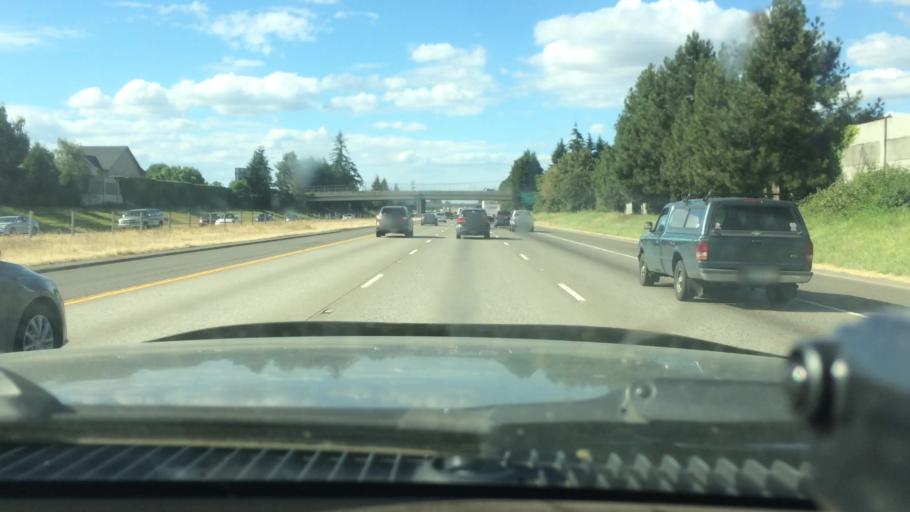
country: US
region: Oregon
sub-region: Marion County
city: Four Corners
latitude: 44.9376
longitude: -122.9902
